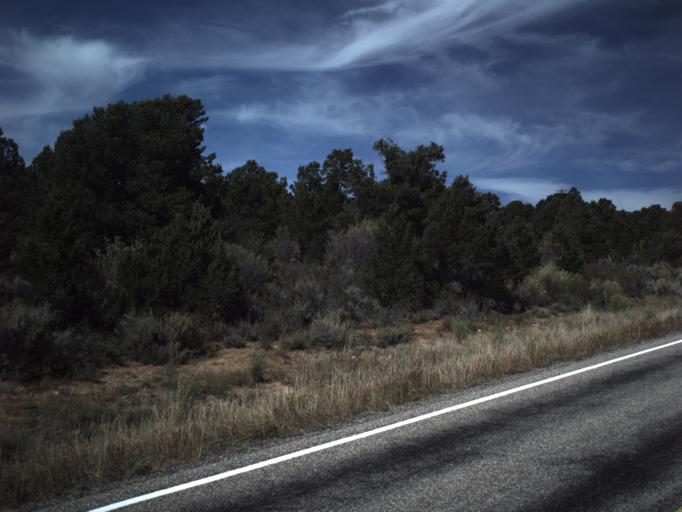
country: US
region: Utah
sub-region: Wayne County
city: Loa
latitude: 37.9684
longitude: -111.4316
